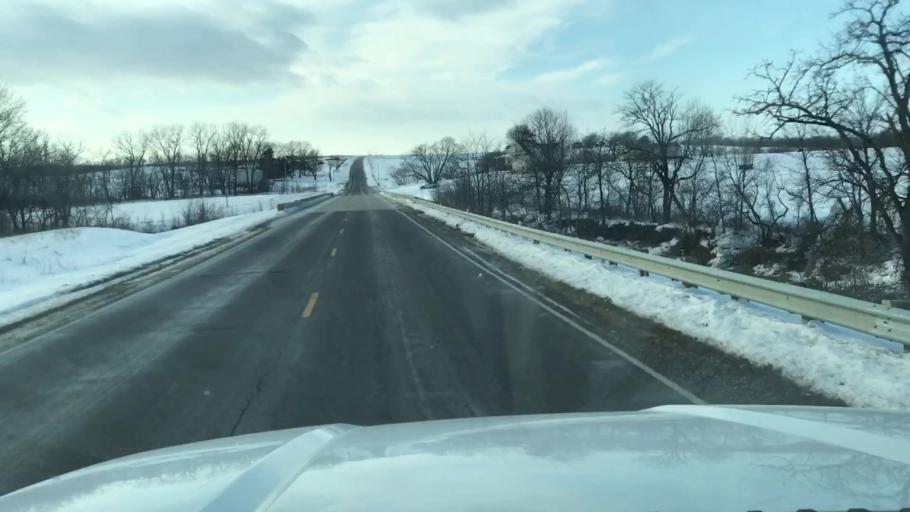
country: US
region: Missouri
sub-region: Nodaway County
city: Maryville
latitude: 40.2008
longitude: -94.8934
